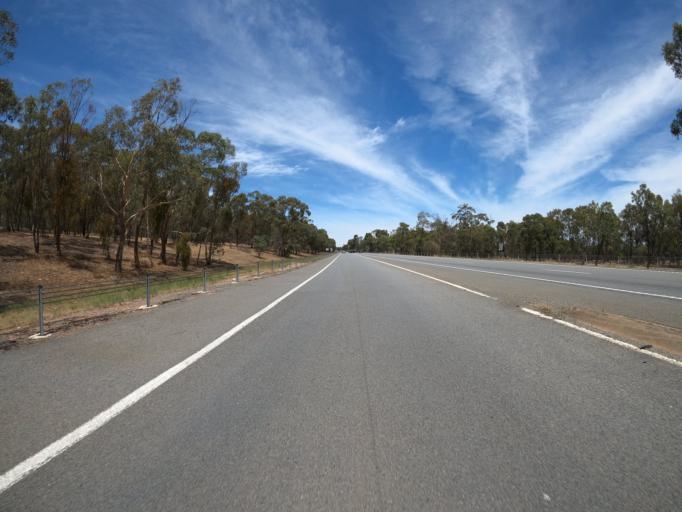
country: AU
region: Victoria
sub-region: Greater Shepparton
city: Shepparton
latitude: -36.7480
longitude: 145.5882
